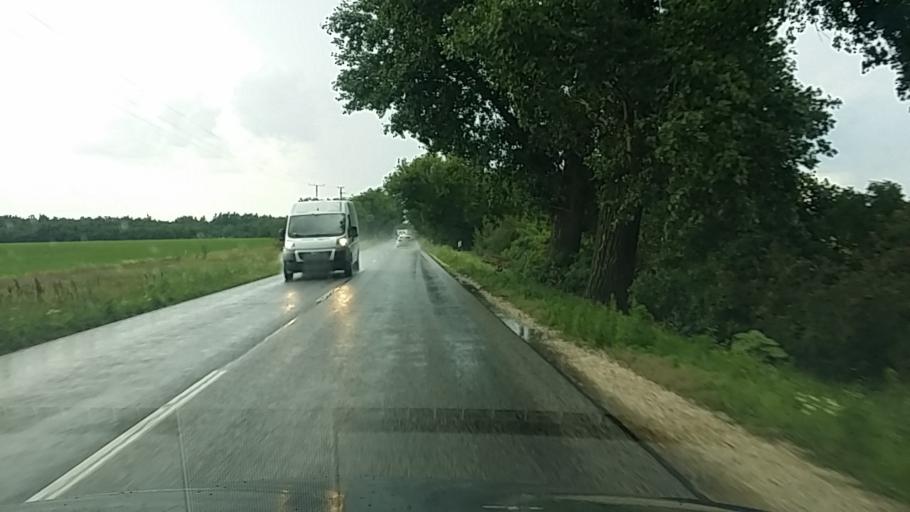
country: HU
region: Pest
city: Felsopakony
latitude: 47.3241
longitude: 19.2999
